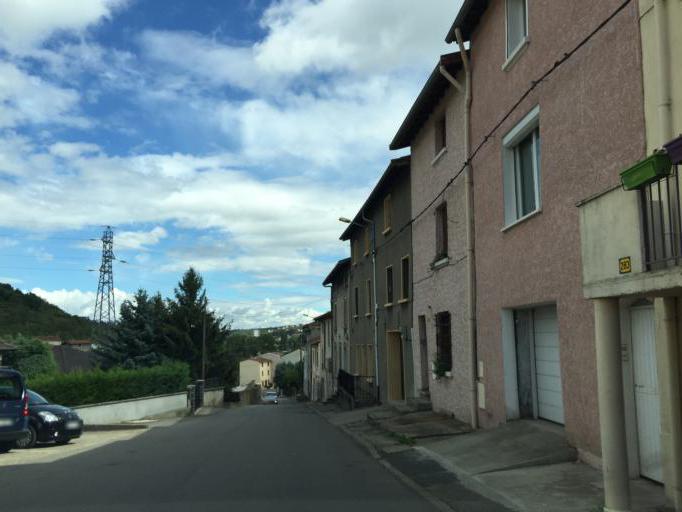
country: FR
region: Rhone-Alpes
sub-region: Departement de la Loire
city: Lorette
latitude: 45.5209
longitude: 4.5894
